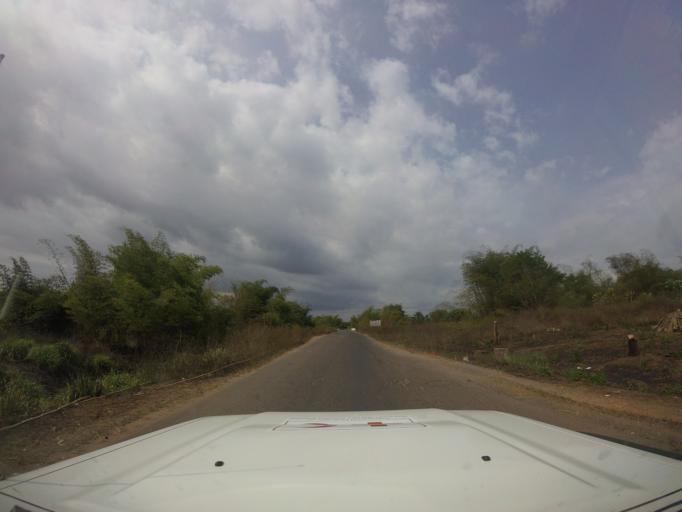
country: LR
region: Montserrado
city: Monrovia
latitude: 6.4904
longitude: -10.8121
